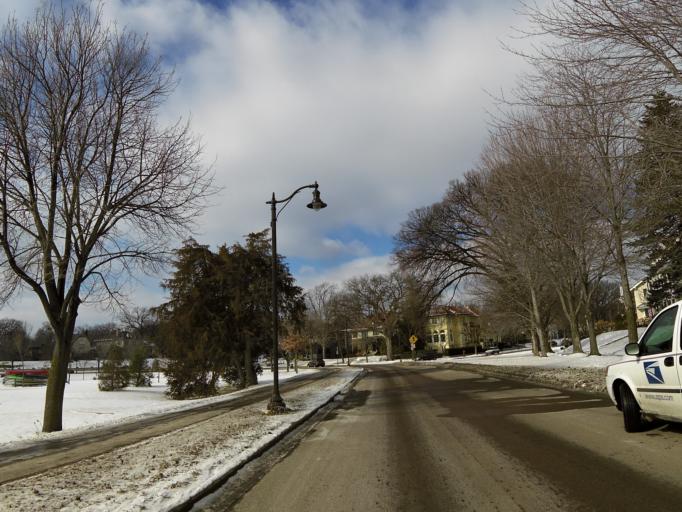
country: US
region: Minnesota
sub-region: Hennepin County
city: Saint Louis Park
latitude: 44.9589
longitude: -93.3080
